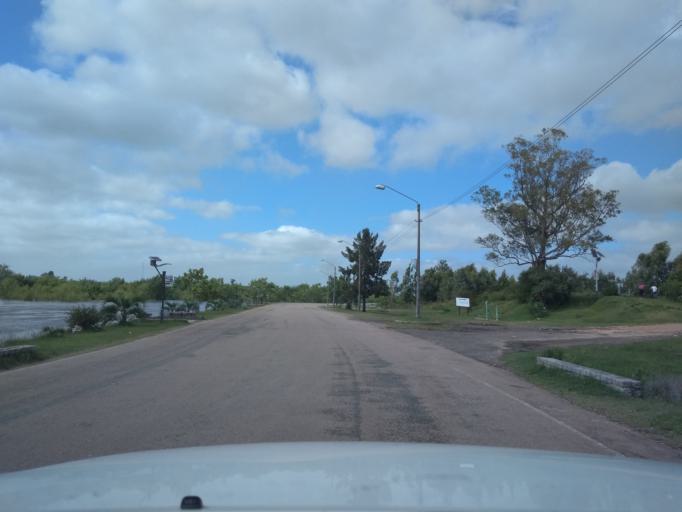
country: UY
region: Florida
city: Florida
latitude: -34.1029
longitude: -56.2037
